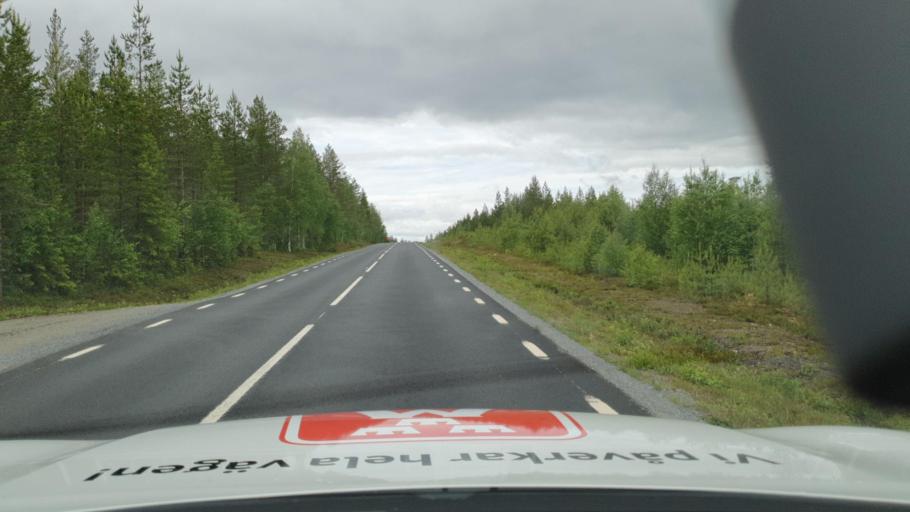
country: SE
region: Vaesterbotten
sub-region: Dorotea Kommun
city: Dorotea
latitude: 64.1901
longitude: 16.6054
